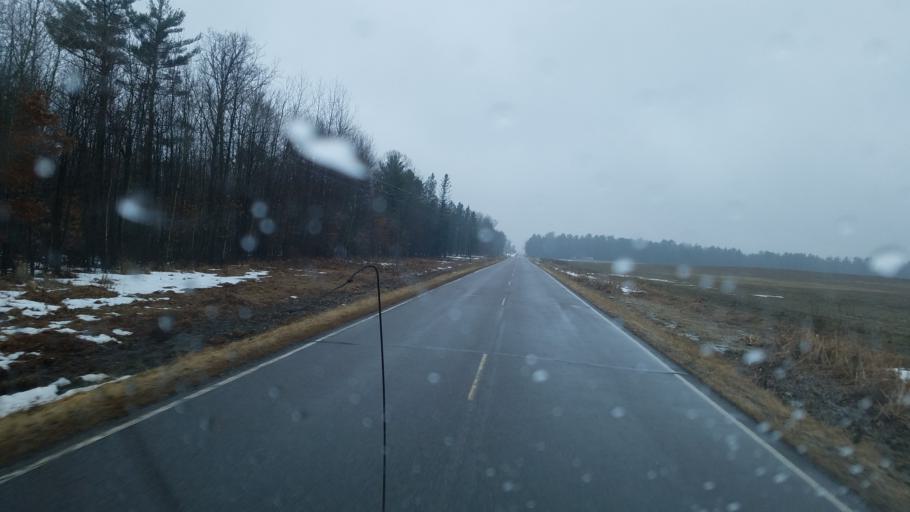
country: US
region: Wisconsin
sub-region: Wood County
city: Marshfield
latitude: 44.4722
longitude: -90.2801
